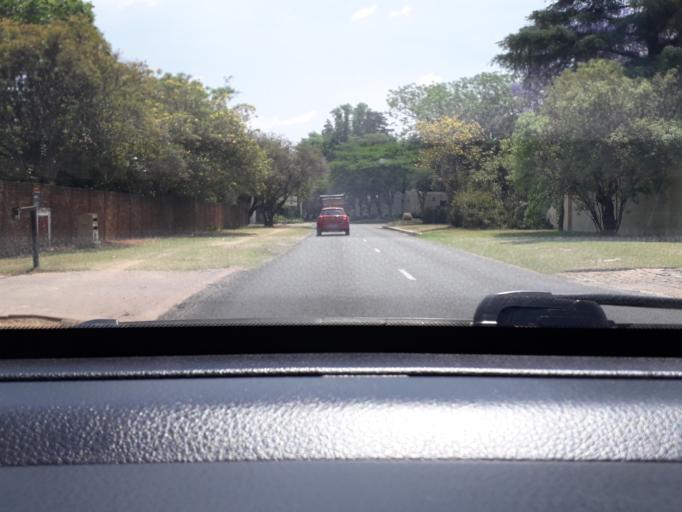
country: ZA
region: Gauteng
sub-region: City of Johannesburg Metropolitan Municipality
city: Midrand
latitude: -26.0431
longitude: 28.0333
